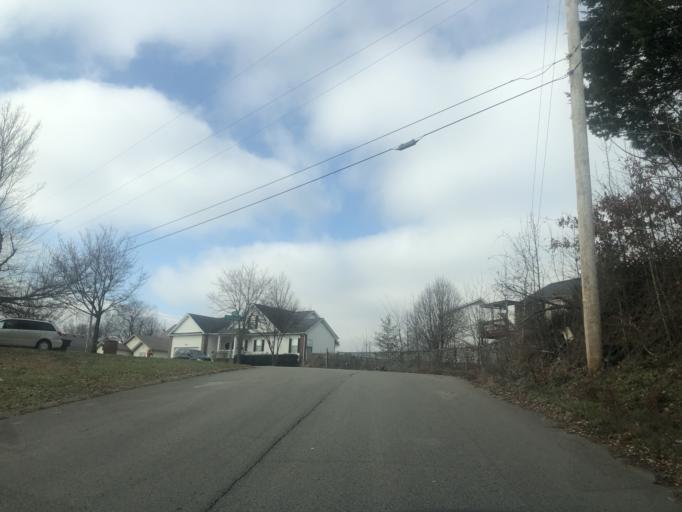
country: US
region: Tennessee
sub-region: Rutherford County
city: La Vergne
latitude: 36.0760
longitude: -86.6495
